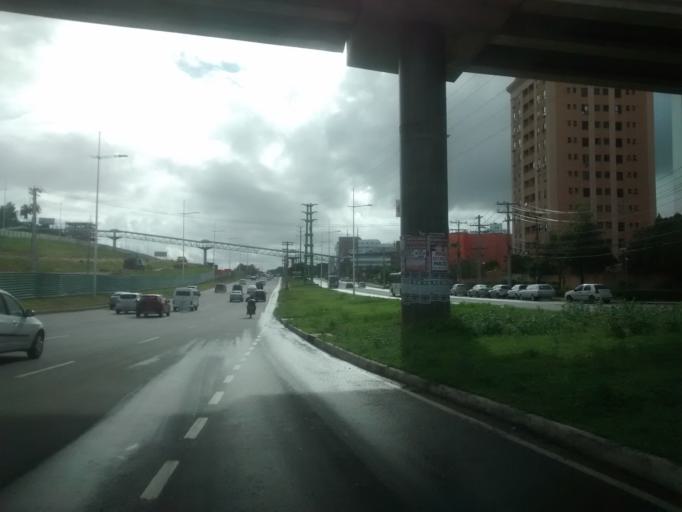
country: BR
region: Bahia
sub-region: Salvador
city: Salvador
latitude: -12.9645
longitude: -38.4356
